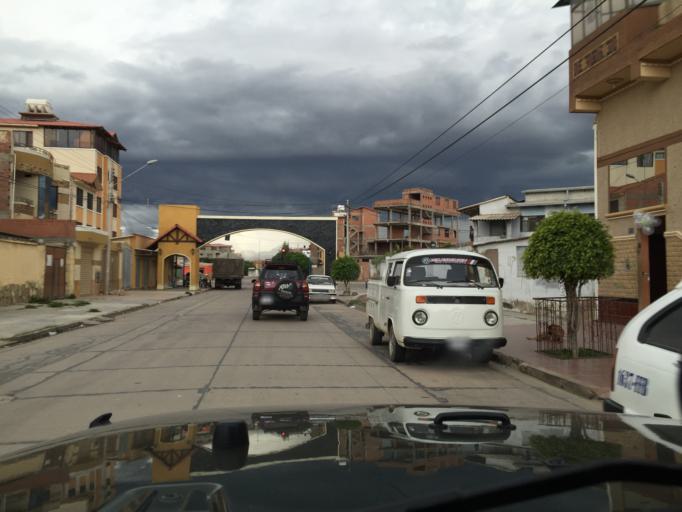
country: BO
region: Cochabamba
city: Cochabamba
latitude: -17.4170
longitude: -66.1640
